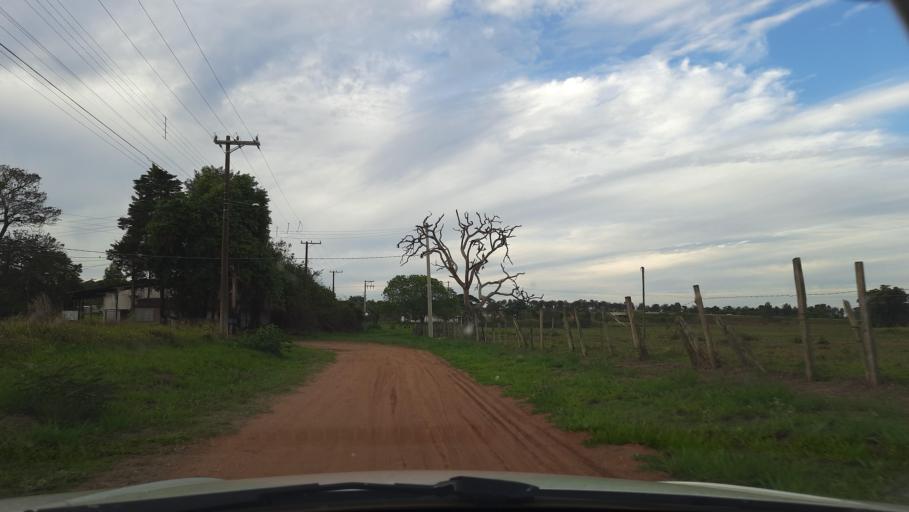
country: BR
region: Sao Paulo
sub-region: Casa Branca
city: Casa Branca
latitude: -21.7770
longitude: -47.0654
